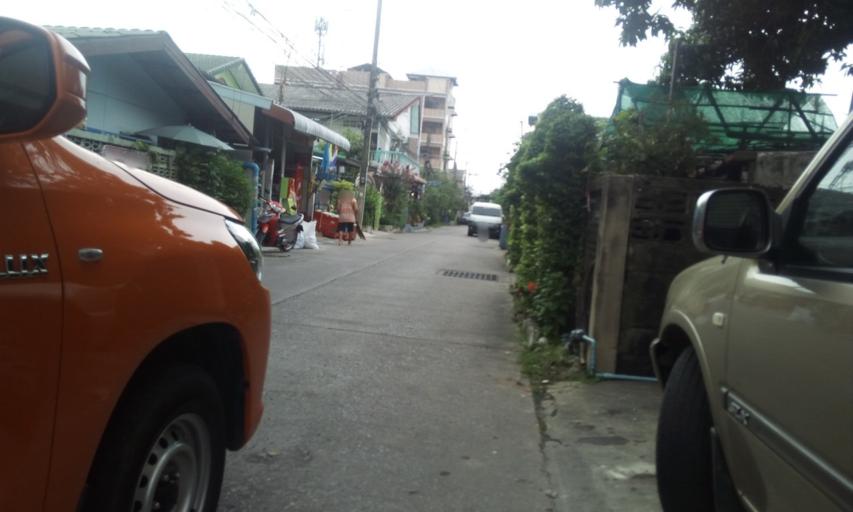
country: TH
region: Bangkok
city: Sai Mai
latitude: 13.9837
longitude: 100.6233
